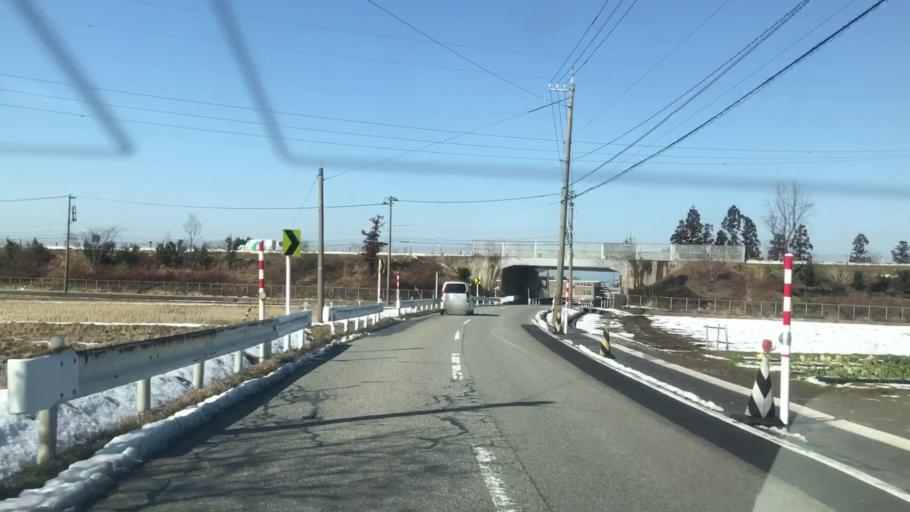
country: JP
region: Toyama
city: Toyama-shi
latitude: 36.6482
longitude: 137.2474
